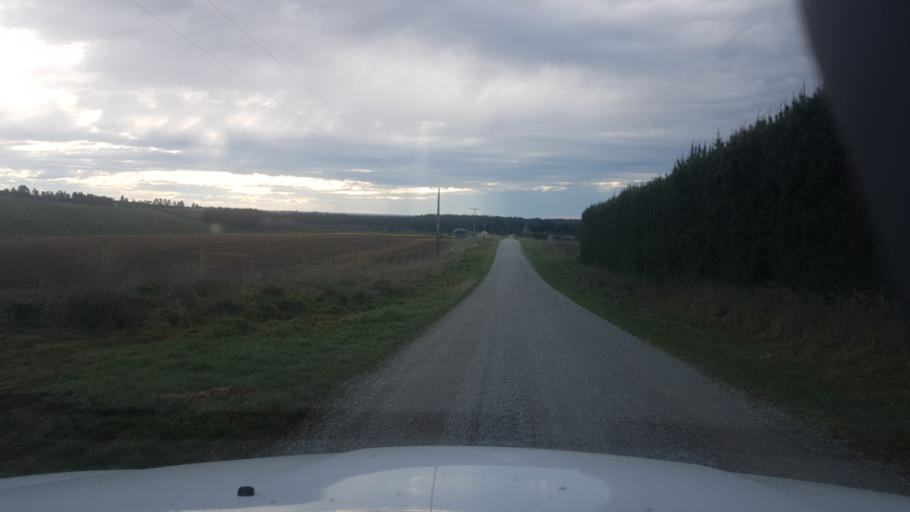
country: NZ
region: Canterbury
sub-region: Timaru District
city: Pleasant Point
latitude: -44.3372
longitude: 171.1489
